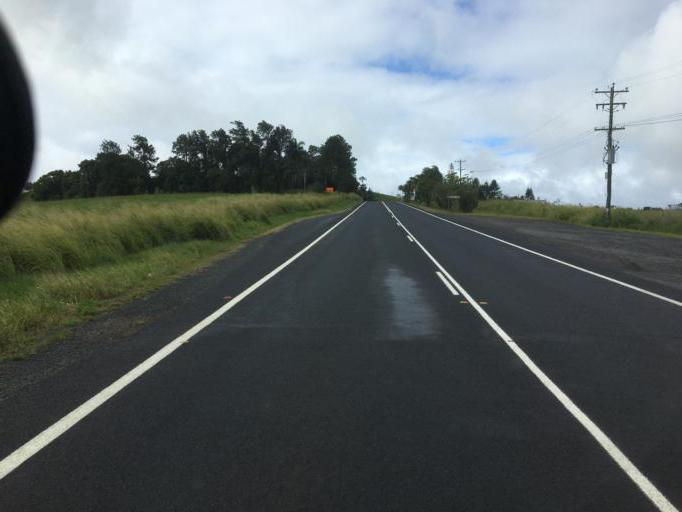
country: AU
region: Queensland
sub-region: Tablelands
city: Ravenshoe
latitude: -17.5058
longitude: 145.6223
